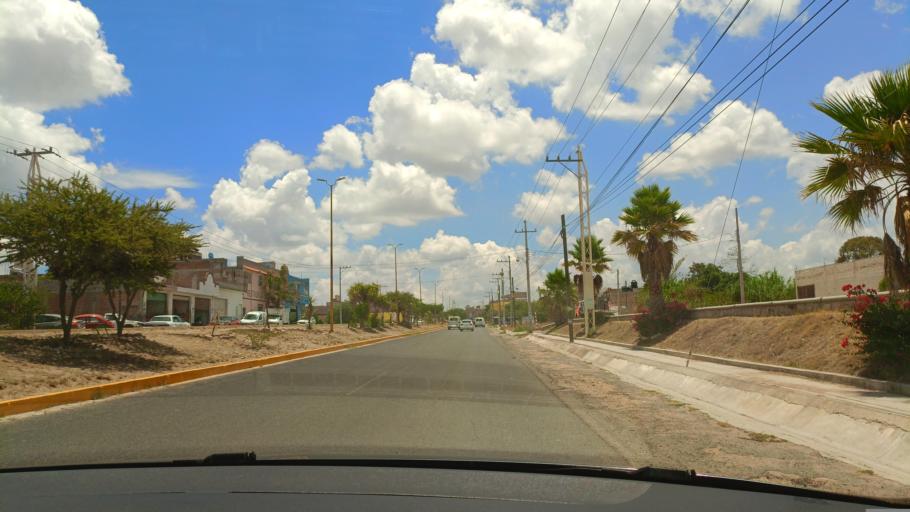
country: MX
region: Guanajuato
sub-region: San Luis de la Paz
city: San Ignacio
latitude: 21.2876
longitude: -100.5283
